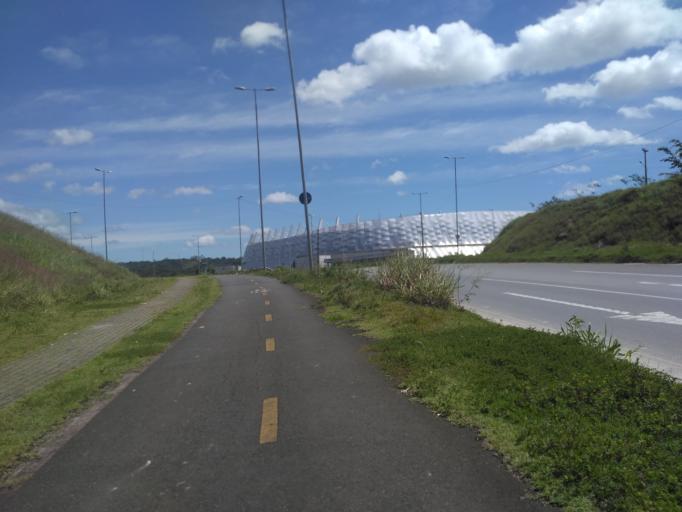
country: BR
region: Pernambuco
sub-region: Sao Lourenco Da Mata
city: Sao Lourenco da Mata
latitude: -8.0430
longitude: -35.0044
